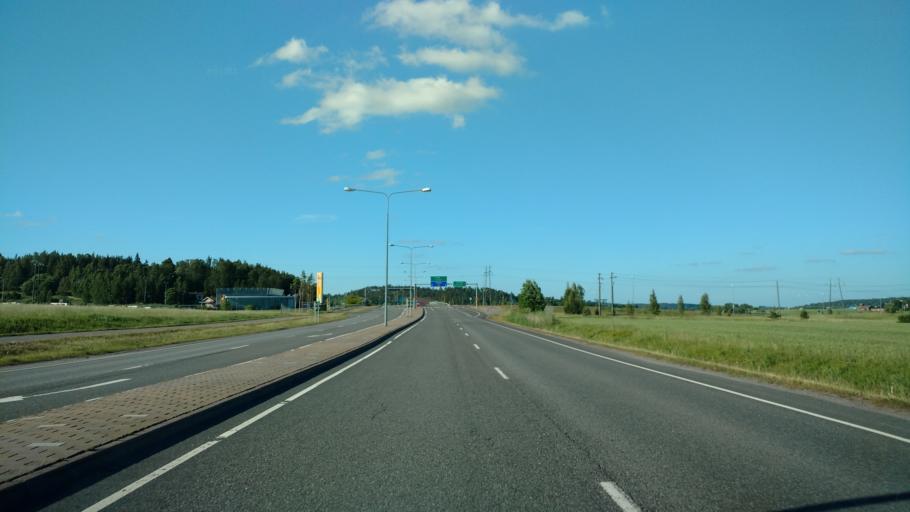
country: FI
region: Varsinais-Suomi
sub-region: Salo
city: Salo
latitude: 60.4149
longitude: 23.1627
